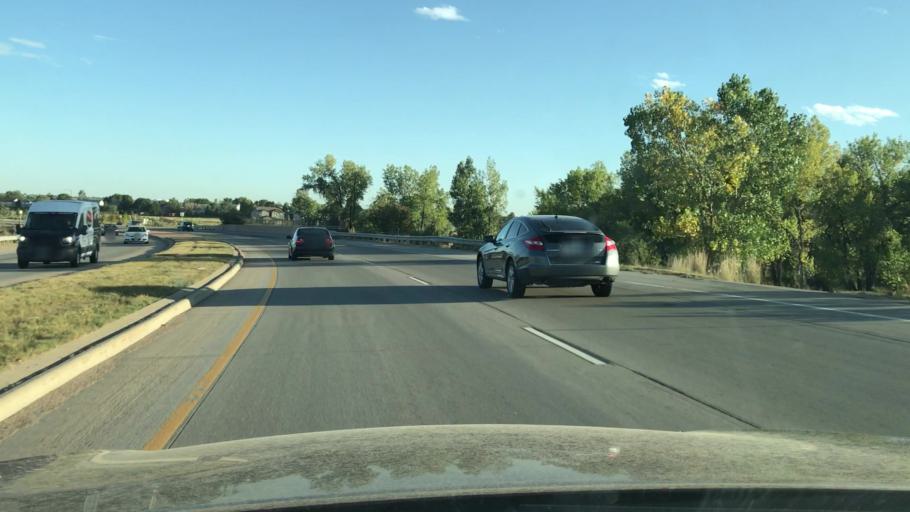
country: US
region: Colorado
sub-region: Boulder County
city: Lafayette
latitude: 39.9809
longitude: -105.0984
